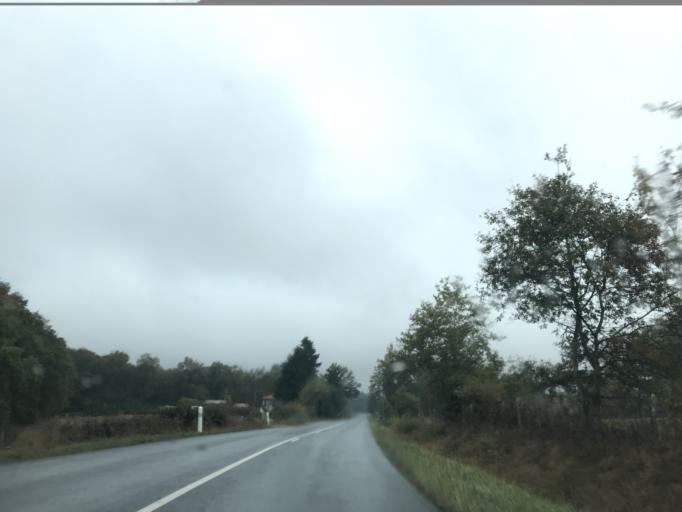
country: FR
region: Auvergne
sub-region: Departement du Puy-de-Dome
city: Peschadoires
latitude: 45.7862
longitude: 3.4535
